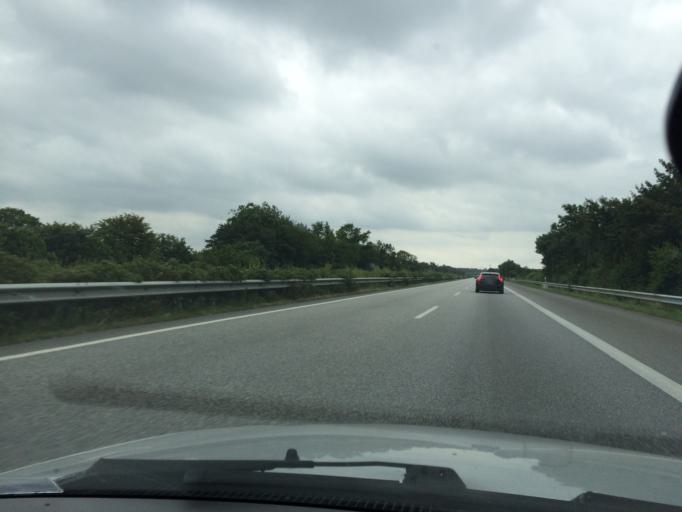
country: DE
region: Schleswig-Holstein
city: Oeversee
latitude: 54.6887
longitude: 9.4118
